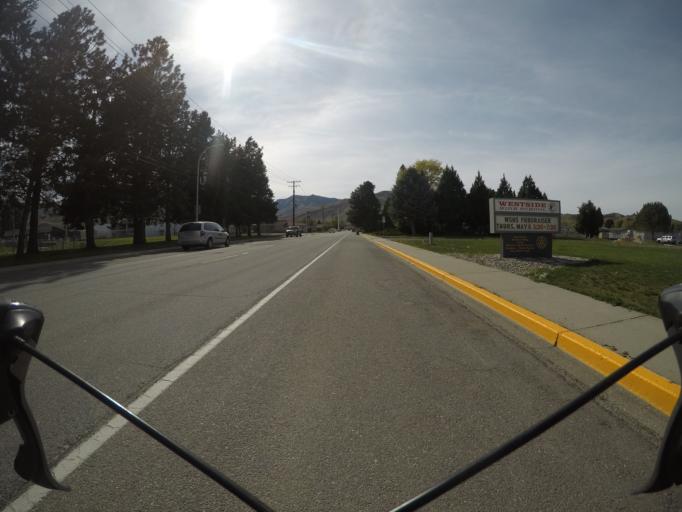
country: US
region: Washington
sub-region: Chelan County
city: West Wenatchee
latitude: 47.4328
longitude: -120.3398
